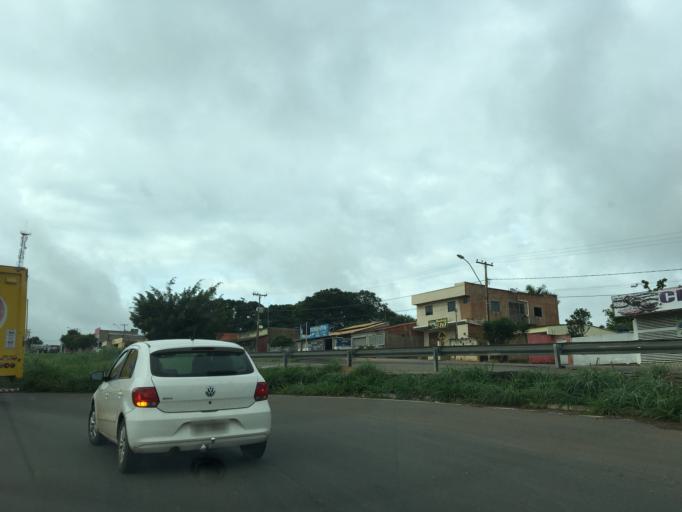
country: BR
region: Goias
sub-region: Luziania
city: Luziania
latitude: -16.0380
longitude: -48.2563
